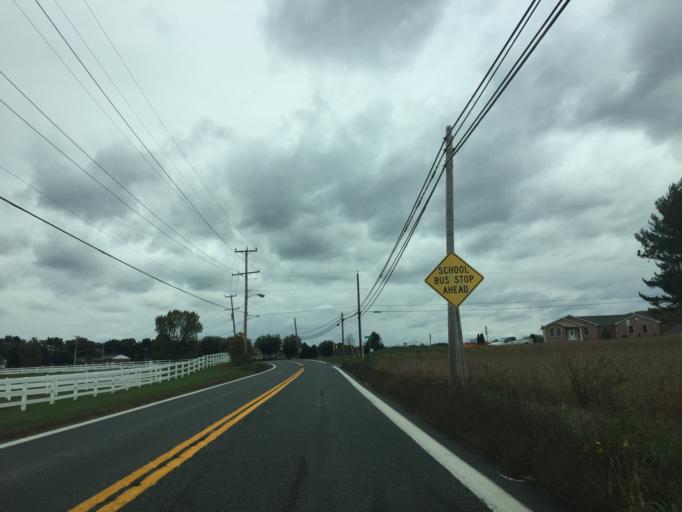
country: US
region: Maryland
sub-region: Harford County
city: Riverside
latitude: 39.5451
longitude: -76.2535
